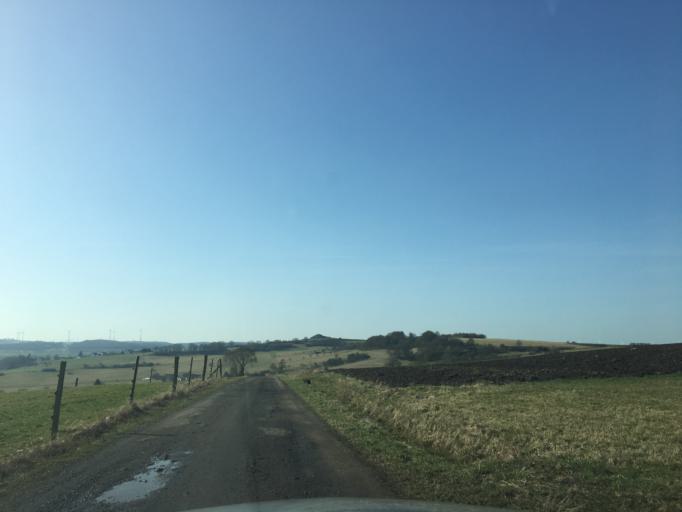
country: DE
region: Hesse
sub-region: Regierungsbezirk Giessen
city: Schwalmtal
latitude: 50.6712
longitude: 9.2700
